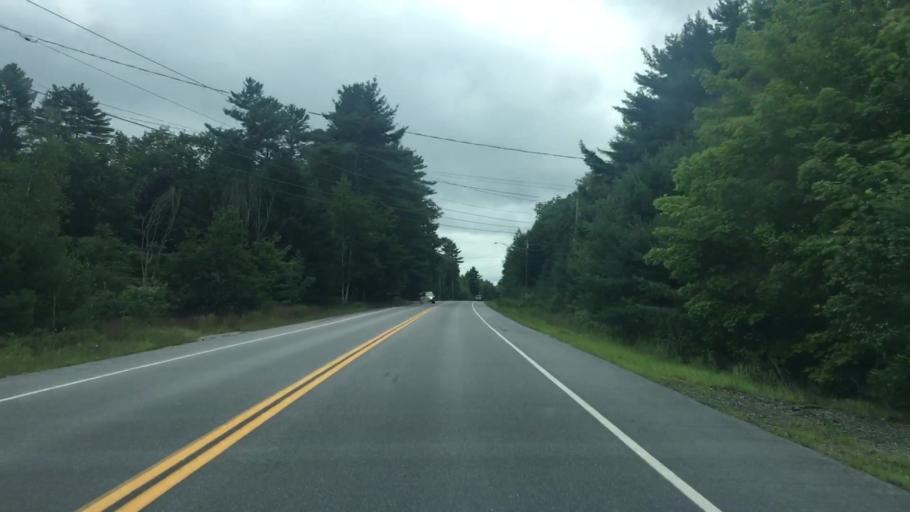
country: US
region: Maine
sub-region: York County
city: Cornish
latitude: 43.7474
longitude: -70.8129
